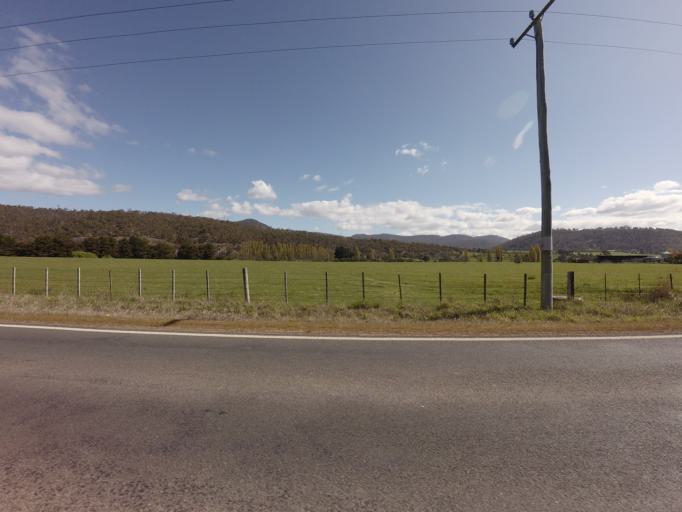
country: AU
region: Tasmania
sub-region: Derwent Valley
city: New Norfolk
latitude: -42.7746
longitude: 147.0358
